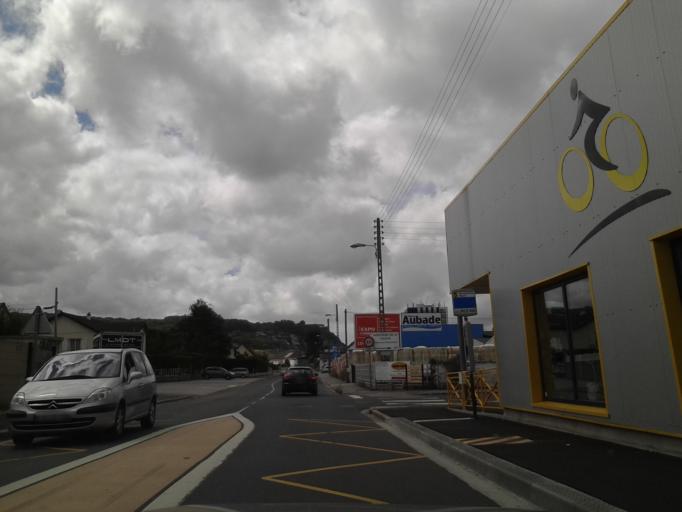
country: FR
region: Lower Normandy
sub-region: Departement de la Manche
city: Cherbourg-Octeville
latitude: 49.6347
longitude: -1.5934
